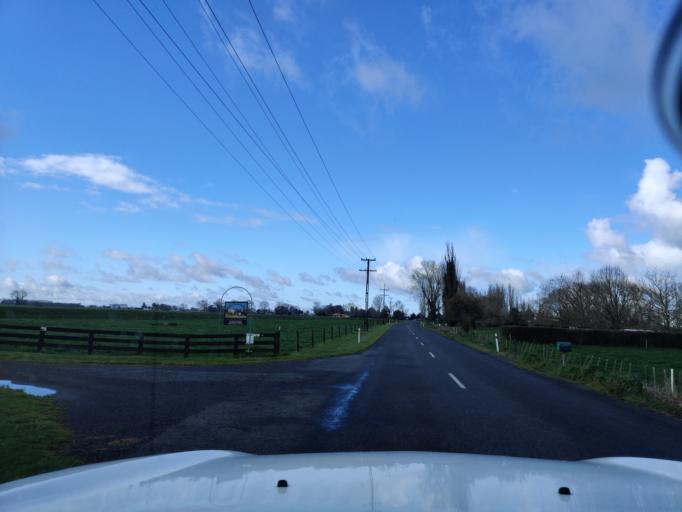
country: NZ
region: Waikato
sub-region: Waikato District
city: Ngaruawahia
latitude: -37.5743
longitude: 175.2674
